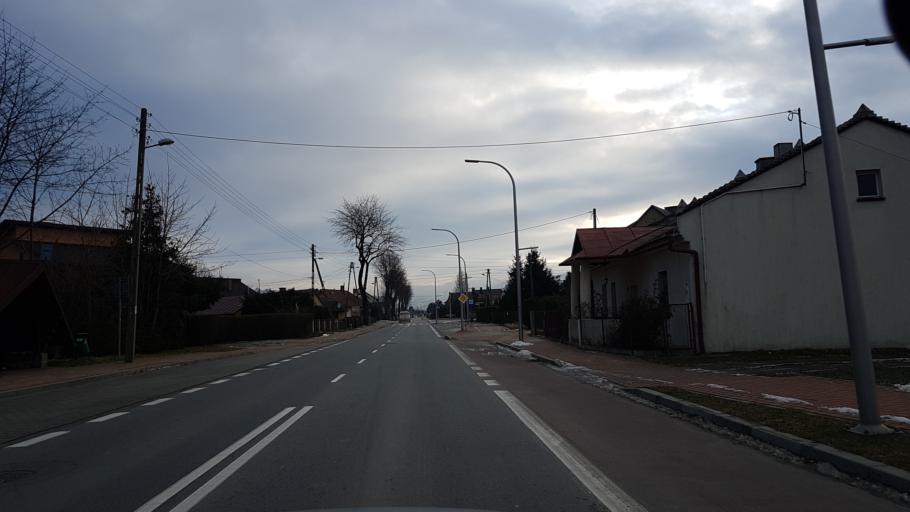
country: PL
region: Lesser Poland Voivodeship
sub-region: Powiat nowosadecki
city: Stary Sacz
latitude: 49.5432
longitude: 20.6440
